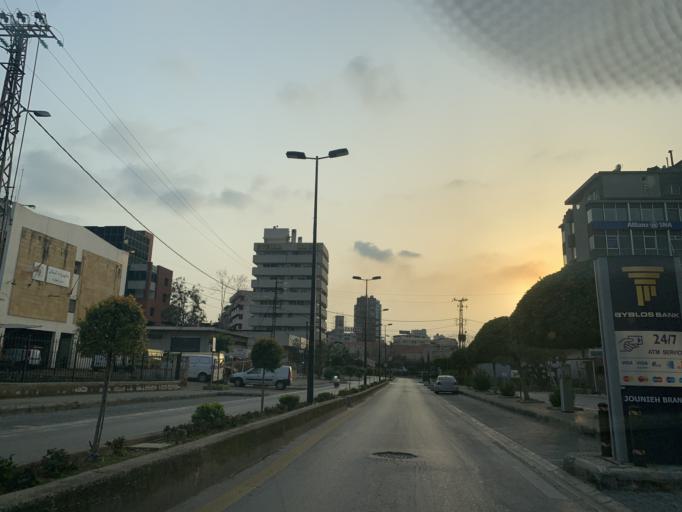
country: LB
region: Mont-Liban
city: Djounie
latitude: 33.9862
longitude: 35.6375
